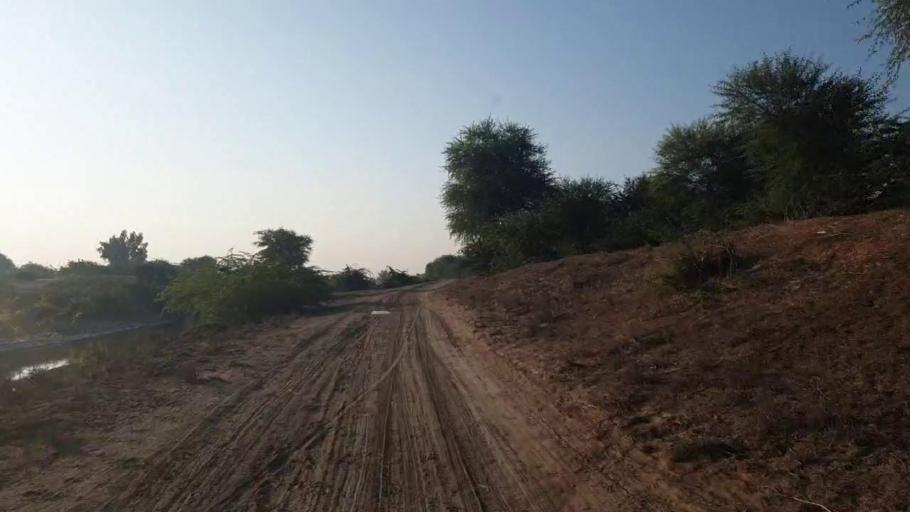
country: PK
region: Sindh
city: Badin
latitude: 24.6452
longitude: 68.7904
